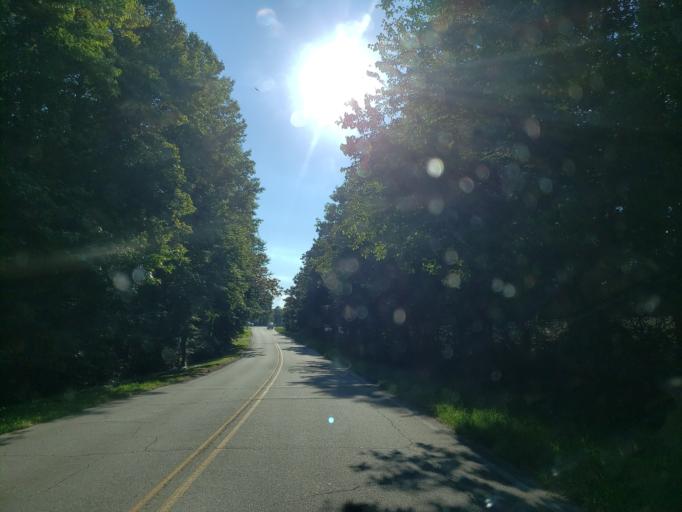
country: US
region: Georgia
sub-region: Haralson County
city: Buchanan
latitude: 33.7874
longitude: -85.1723
